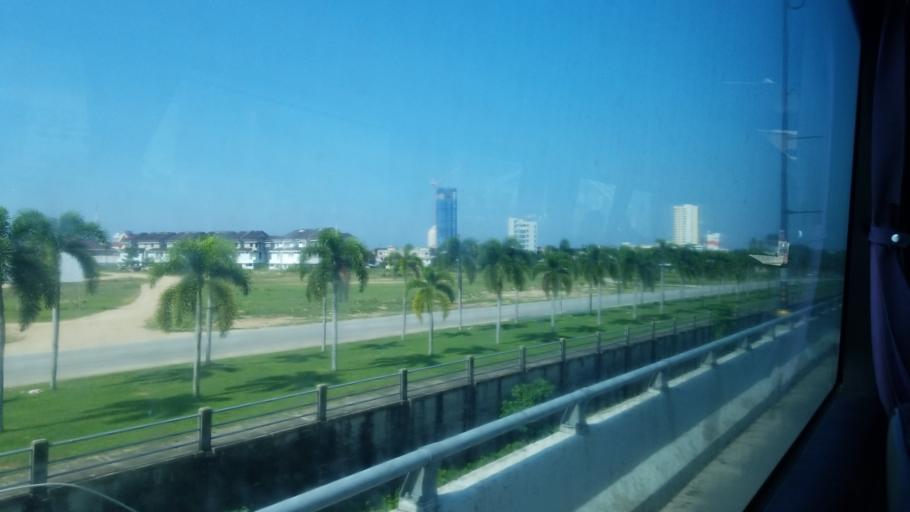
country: MY
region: Kelantan
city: Kota Bharu
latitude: 6.1161
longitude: 102.2310
